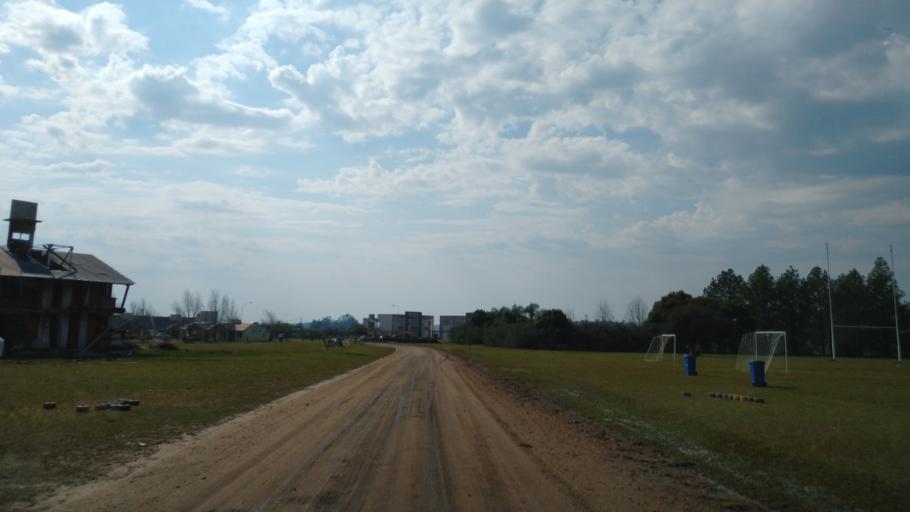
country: AR
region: Entre Rios
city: Chajari
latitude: -30.7450
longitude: -58.0112
